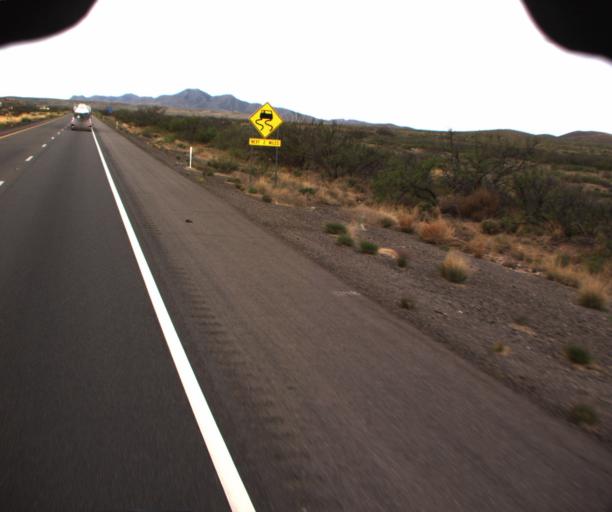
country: US
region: Arizona
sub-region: Cochise County
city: Willcox
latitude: 32.1570
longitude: -109.9825
